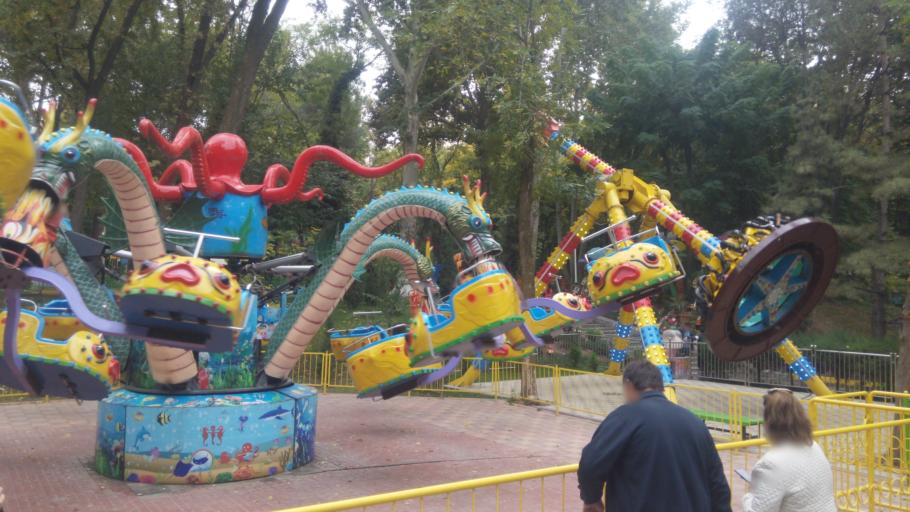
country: UZ
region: Toshkent Shahri
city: Tashkent
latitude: 41.2825
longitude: 69.2164
